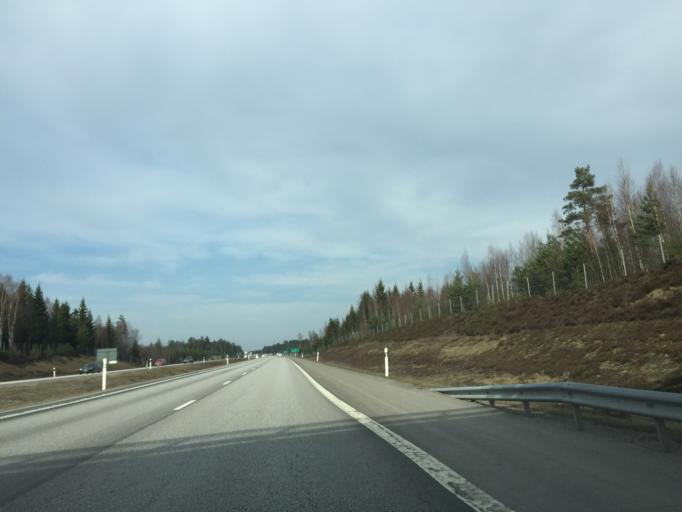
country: SE
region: OErebro
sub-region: Lindesbergs Kommun
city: Fellingsbro
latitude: 59.3449
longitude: 15.5492
